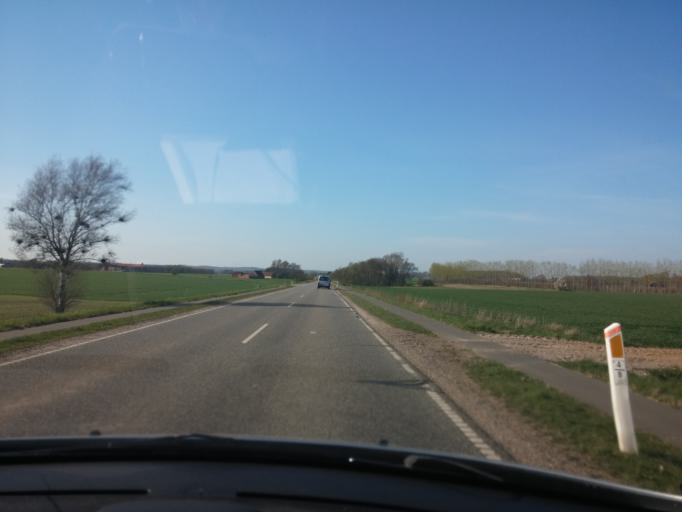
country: DK
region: Central Jutland
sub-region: Odder Kommune
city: Odder
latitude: 55.9432
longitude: 10.2090
